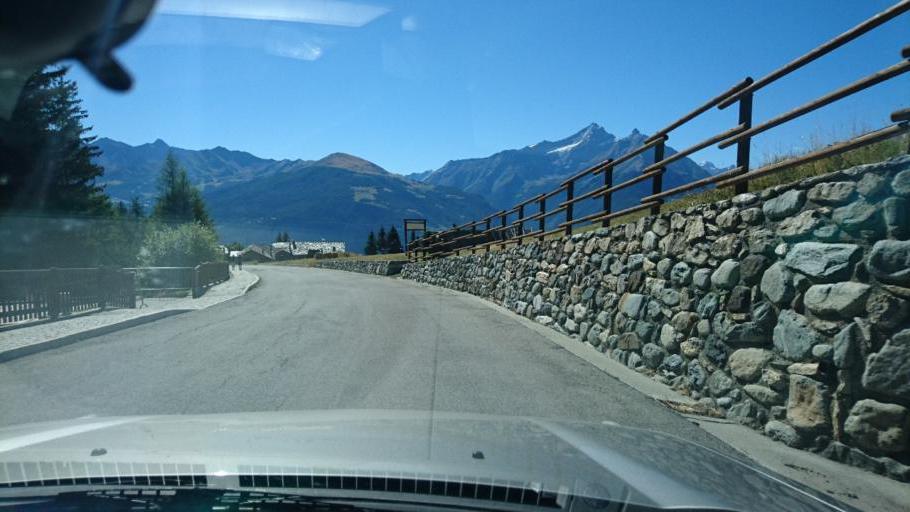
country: IT
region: Aosta Valley
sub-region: Valle d'Aosta
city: Saint-Nicolas
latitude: 45.7317
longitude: 7.1872
